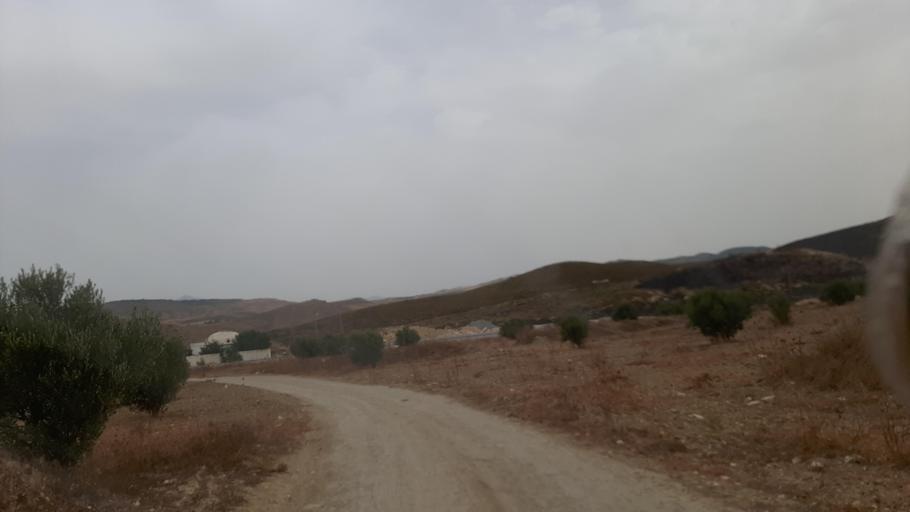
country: TN
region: Tunis
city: La Mohammedia
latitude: 36.5651
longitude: 10.1492
